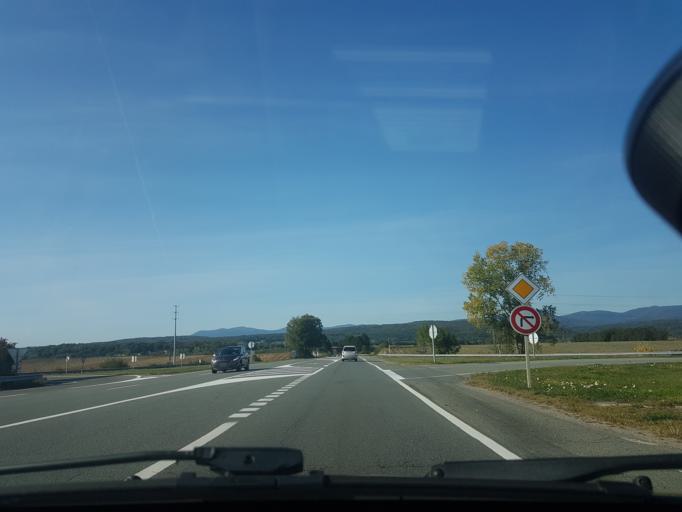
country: FR
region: Franche-Comte
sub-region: Territoire de Belfort
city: Chevremont
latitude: 47.6490
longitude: 6.9160
